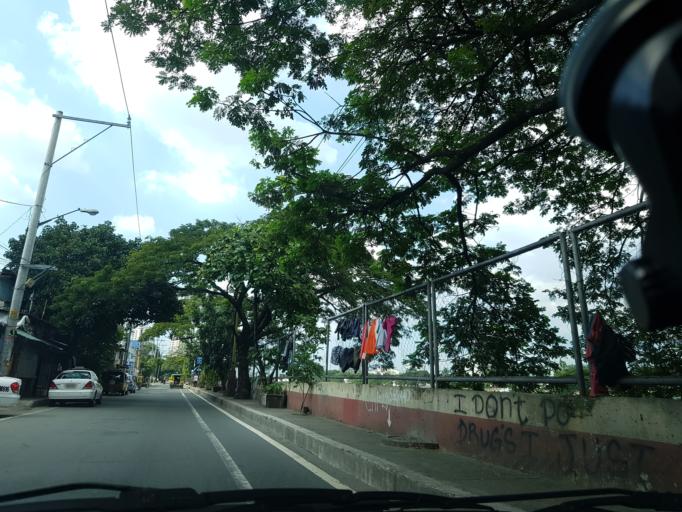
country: PH
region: Metro Manila
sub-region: Marikina
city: Calumpang
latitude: 14.5938
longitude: 121.0912
